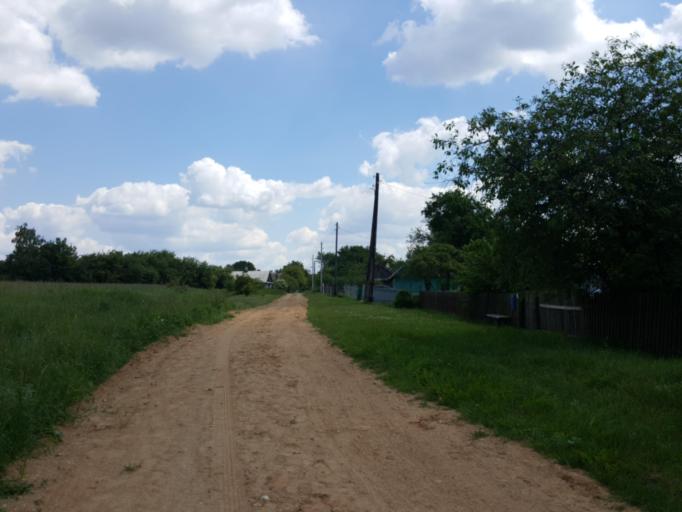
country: BY
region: Brest
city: Kamyanyets
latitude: 52.4429
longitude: 23.7245
